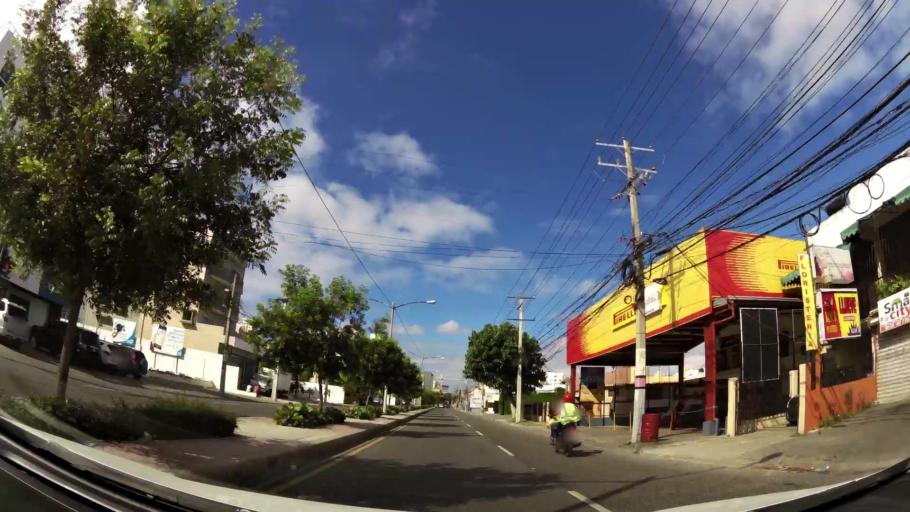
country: DO
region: Nacional
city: Bella Vista
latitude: 18.4550
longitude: -69.9444
